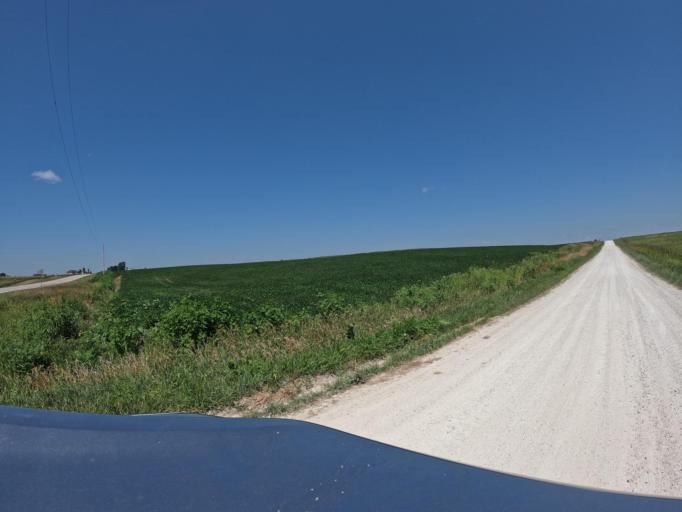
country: US
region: Iowa
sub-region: Keokuk County
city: Sigourney
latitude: 41.2651
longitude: -92.2191
